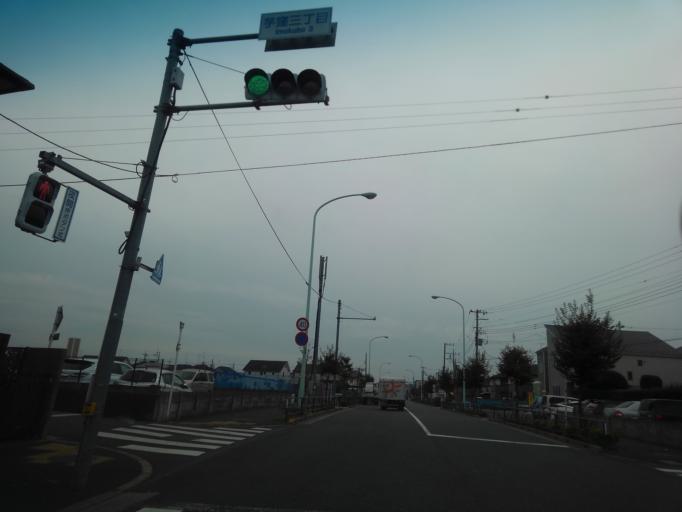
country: JP
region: Tokyo
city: Higashimurayama-shi
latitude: 35.7532
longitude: 139.4158
